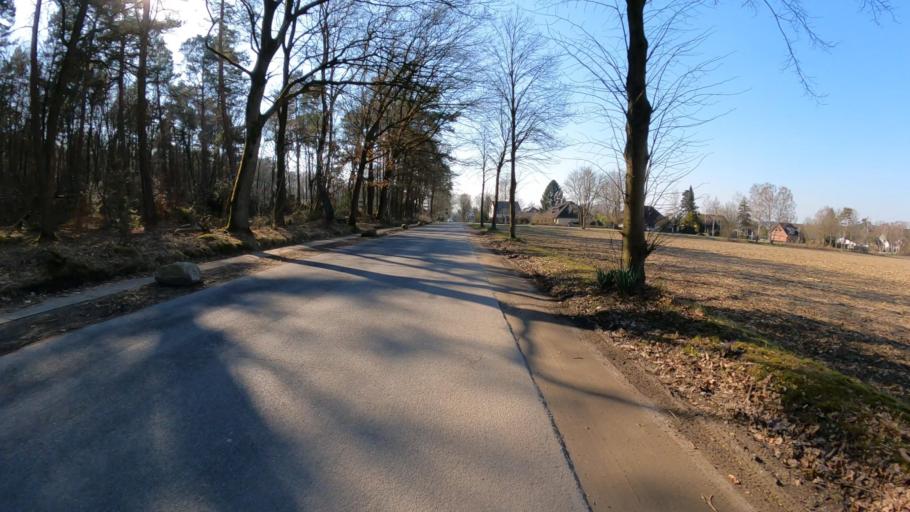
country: DE
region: Lower Saxony
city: Buchholz in der Nordheide
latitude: 53.3096
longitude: 9.8243
